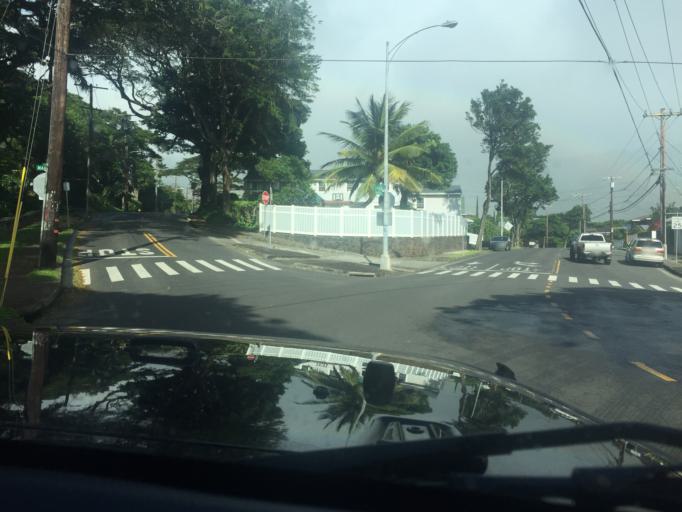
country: US
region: Hawaii
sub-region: Honolulu County
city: Honolulu
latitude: 21.3153
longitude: -157.8121
